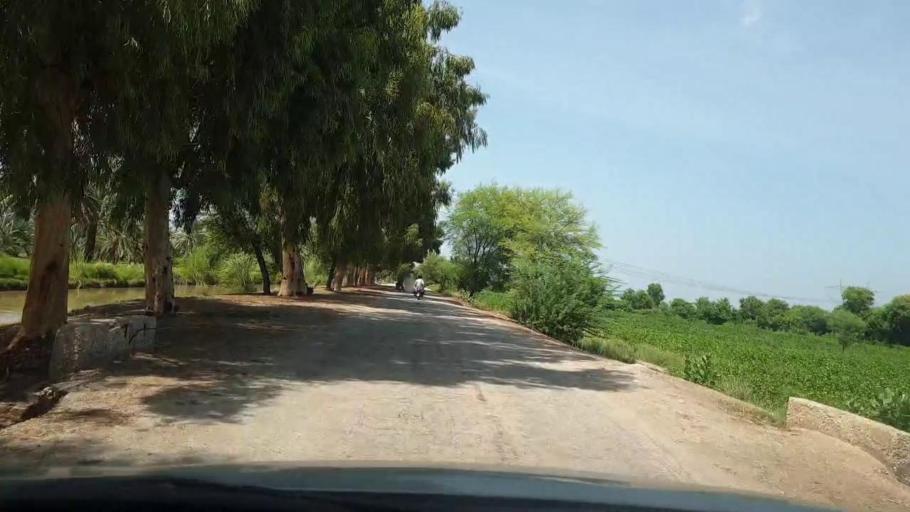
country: PK
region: Sindh
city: Pano Aqil
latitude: 27.7011
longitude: 69.1123
